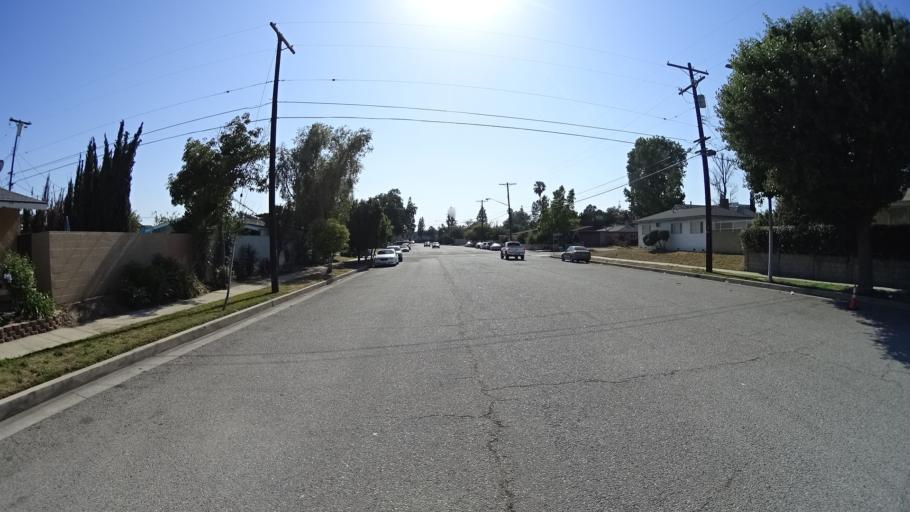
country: US
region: California
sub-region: Los Angeles County
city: Van Nuys
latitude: 34.2158
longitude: -118.4261
